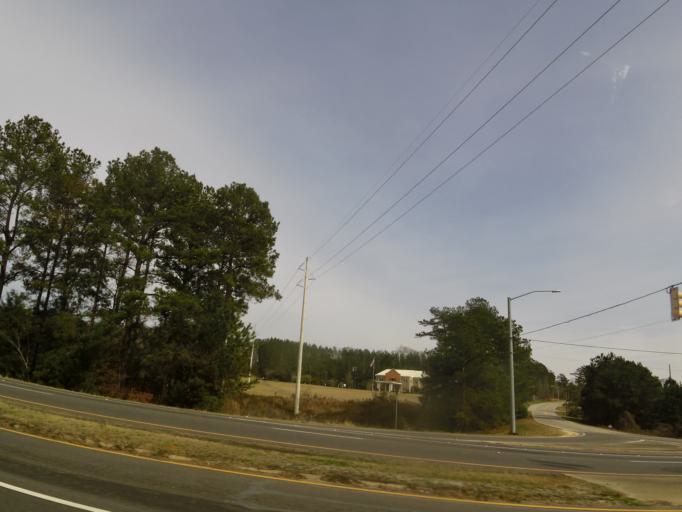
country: US
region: Alabama
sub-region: Dale County
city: Ozark
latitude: 31.4726
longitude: -85.6789
